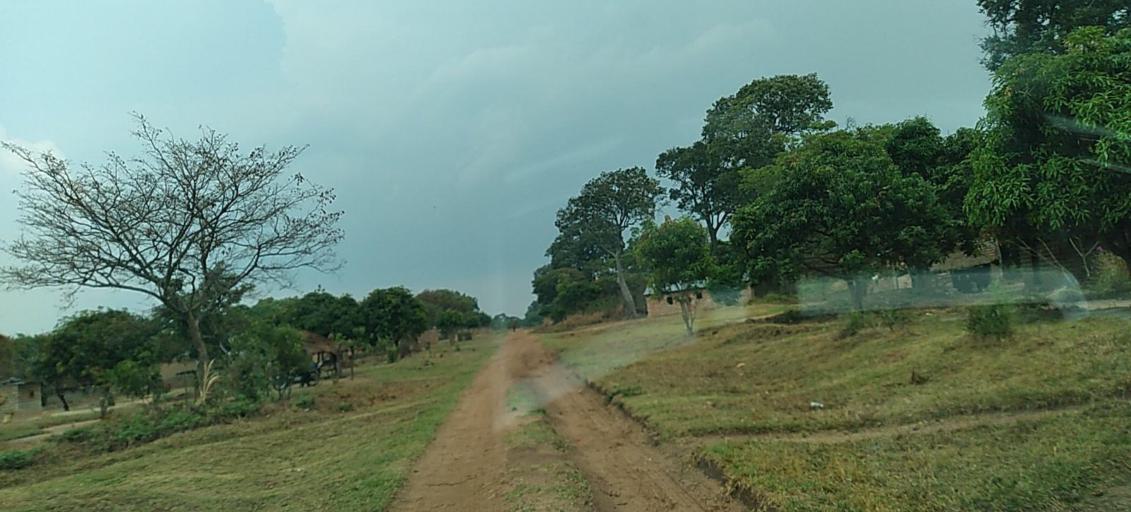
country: ZM
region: North-Western
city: Mwinilunga
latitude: -11.4480
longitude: 24.5906
